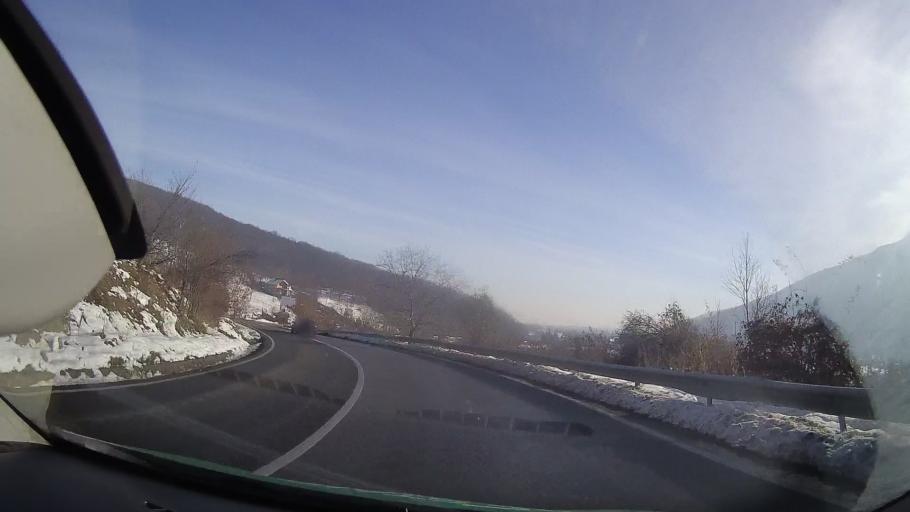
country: RO
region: Neamt
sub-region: Comuna Garcina
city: Garcina
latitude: 46.9775
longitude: 26.3576
